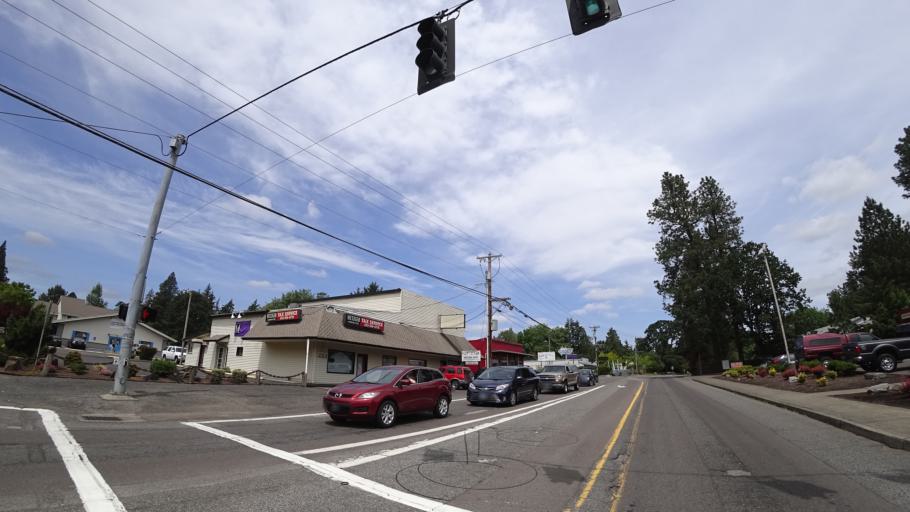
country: US
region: Oregon
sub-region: Washington County
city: Metzger
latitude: 45.4466
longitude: -122.7656
